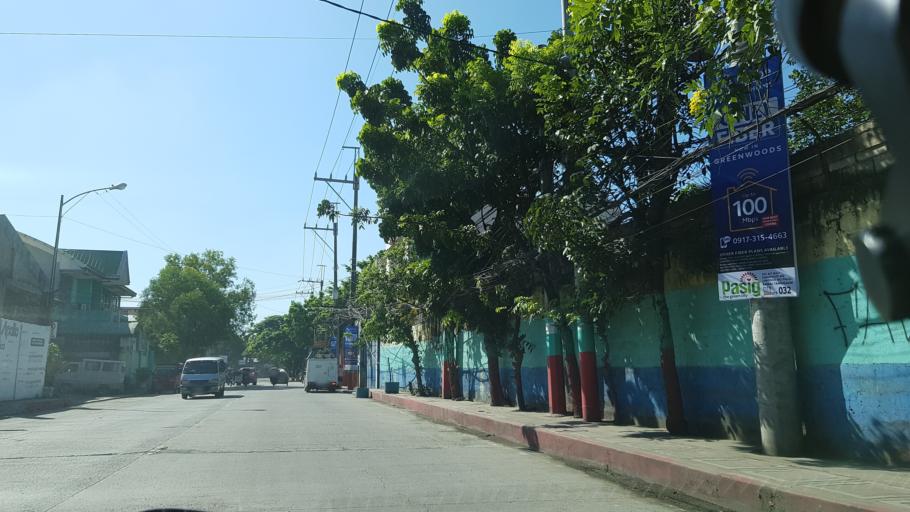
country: PH
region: Calabarzon
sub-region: Province of Rizal
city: Pateros
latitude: 14.5598
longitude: 121.0952
